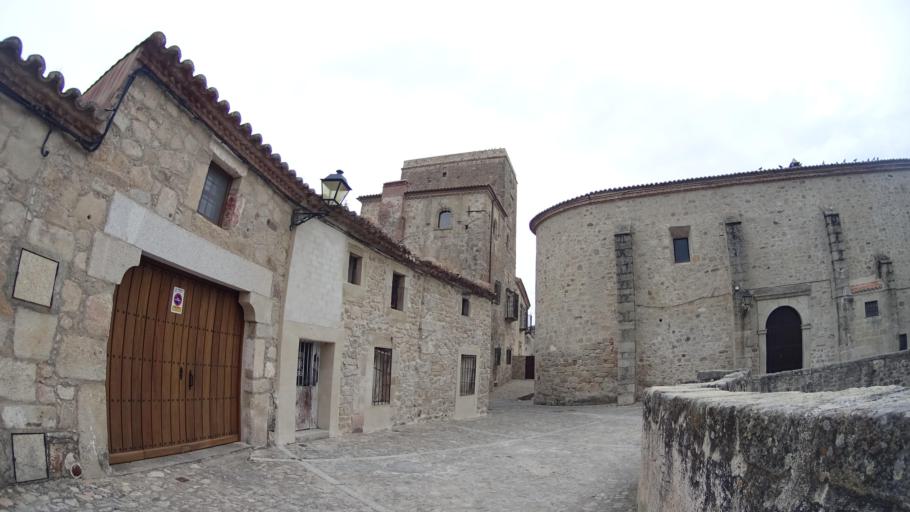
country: ES
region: Extremadura
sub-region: Provincia de Caceres
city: Trujillo
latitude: 39.4597
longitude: -5.8849
